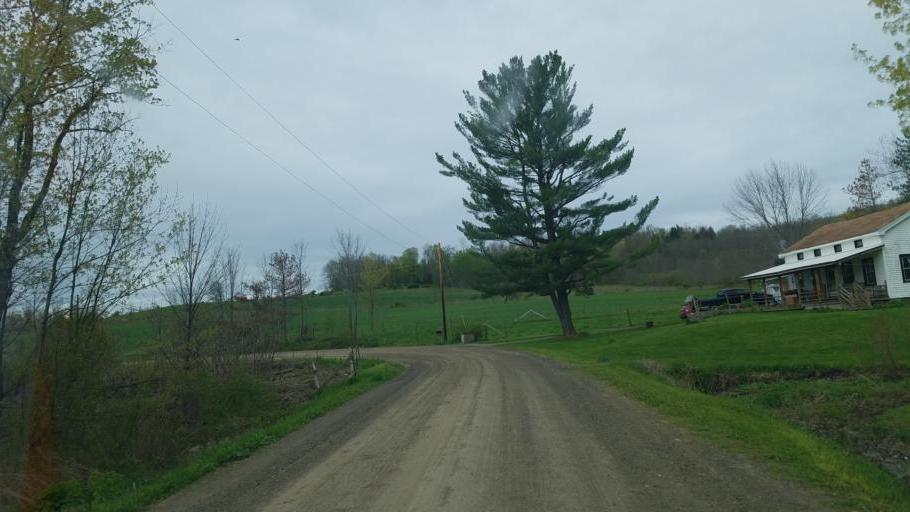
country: US
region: Pennsylvania
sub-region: Tioga County
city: Westfield
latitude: 42.0574
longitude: -77.4851
